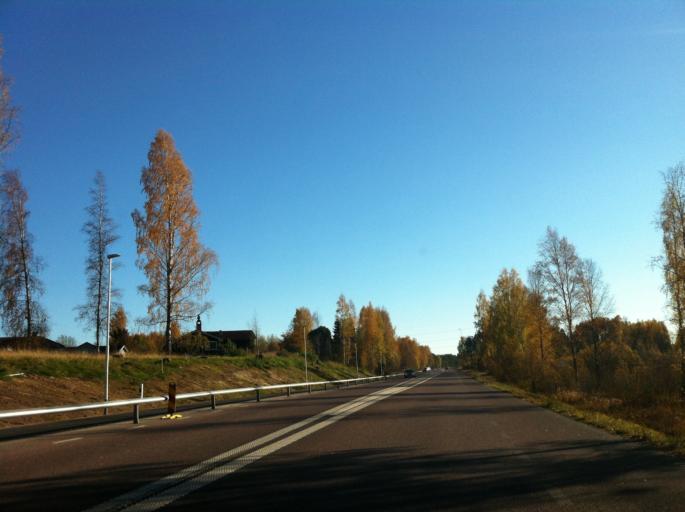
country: SE
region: Dalarna
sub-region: Mora Kommun
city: Mora
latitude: 61.0279
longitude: 14.5300
